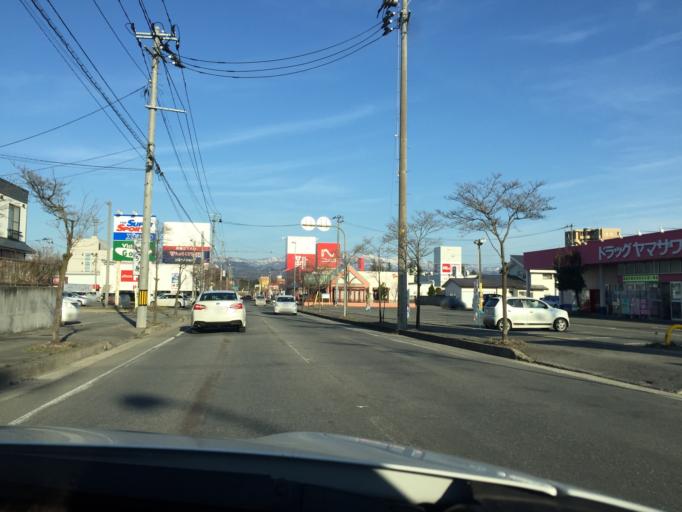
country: JP
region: Yamagata
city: Yonezawa
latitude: 37.9261
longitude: 140.1143
